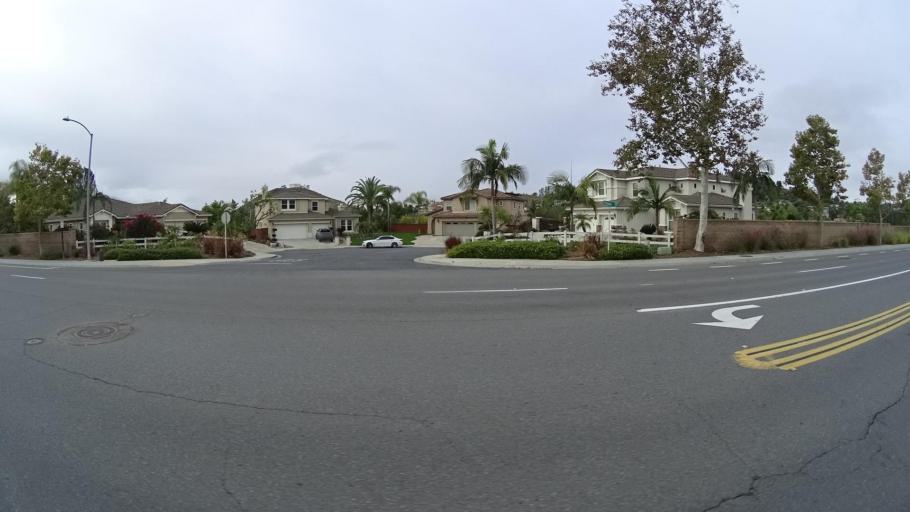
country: US
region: California
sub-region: San Diego County
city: Rancho San Diego
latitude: 32.7667
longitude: -116.9240
